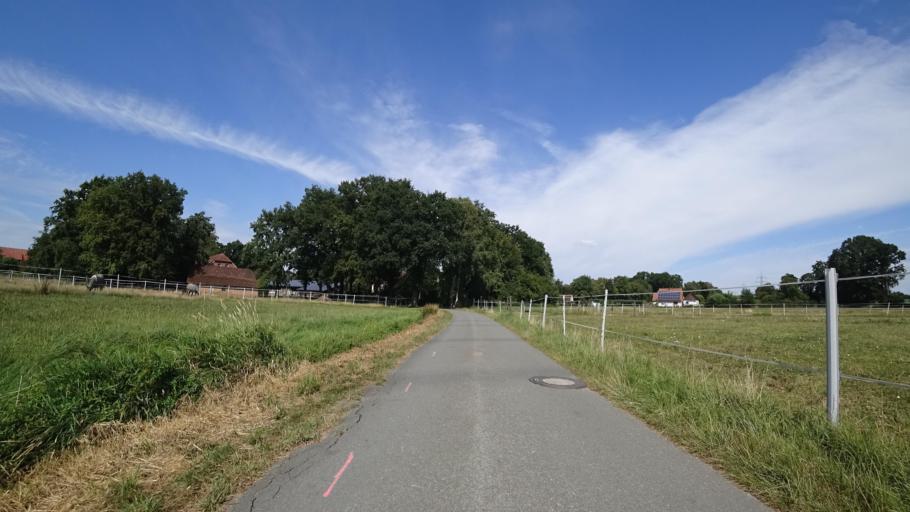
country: DE
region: North Rhine-Westphalia
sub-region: Regierungsbezirk Detmold
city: Guetersloh
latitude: 51.9527
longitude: 8.3879
